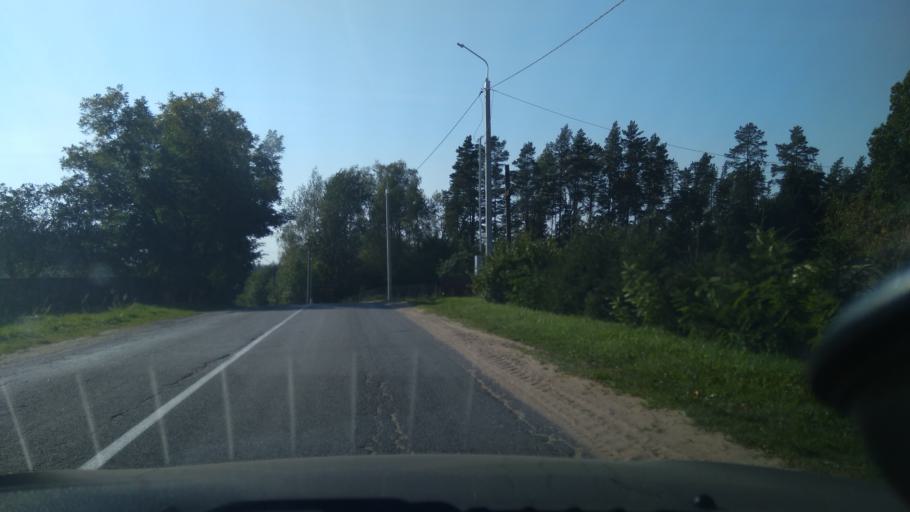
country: BY
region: Minsk
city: Rakaw
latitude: 54.0034
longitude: 27.0461
